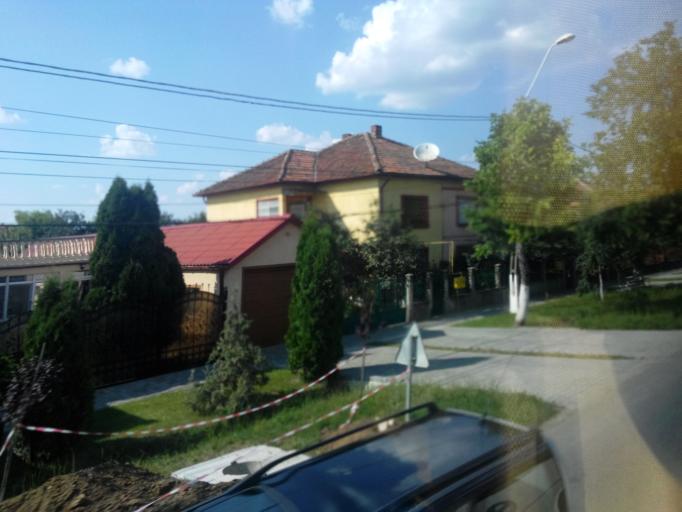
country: RO
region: Timis
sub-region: Comuna Dumbravita
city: Dumbravita
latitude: 45.7974
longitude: 21.2429
